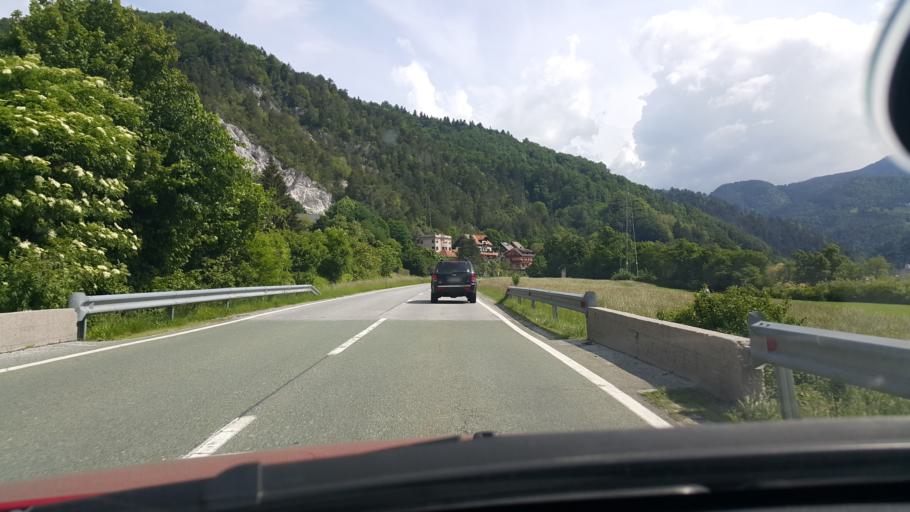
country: SI
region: Trzic
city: Bistrica pri Trzicu
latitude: 46.3564
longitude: 14.2943
